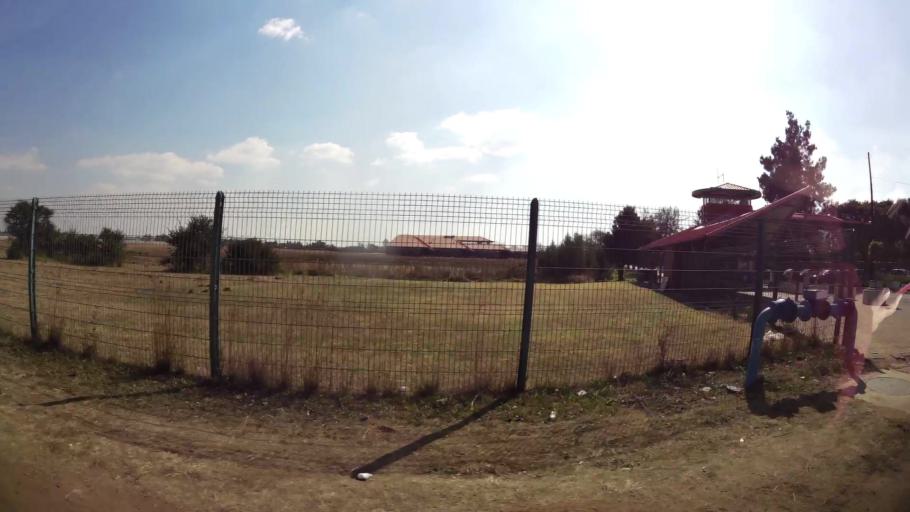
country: ZA
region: Gauteng
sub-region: Ekurhuleni Metropolitan Municipality
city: Benoni
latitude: -26.1445
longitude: 28.3975
